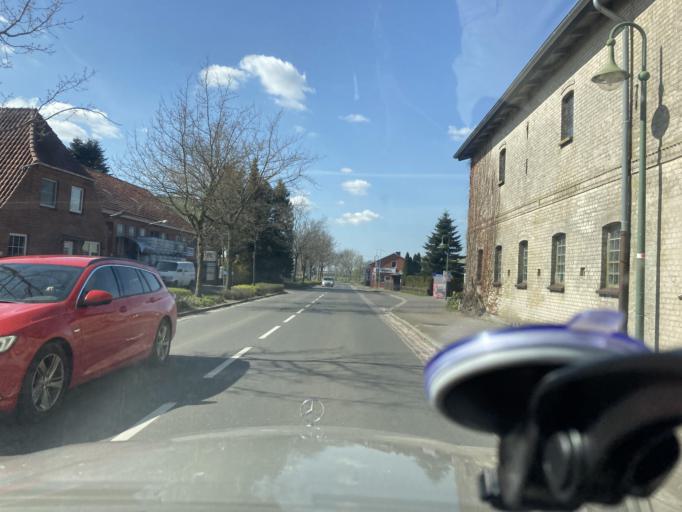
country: DE
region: Schleswig-Holstein
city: Weddingstedt
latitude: 54.2385
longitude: 9.0863
